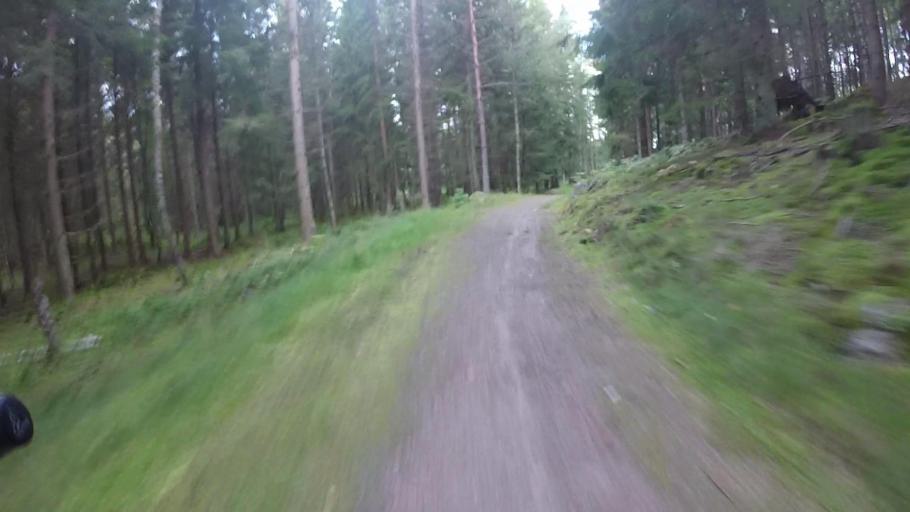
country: SE
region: Vaestra Goetaland
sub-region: Trollhattan
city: Trollhattan
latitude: 58.2565
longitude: 12.2385
